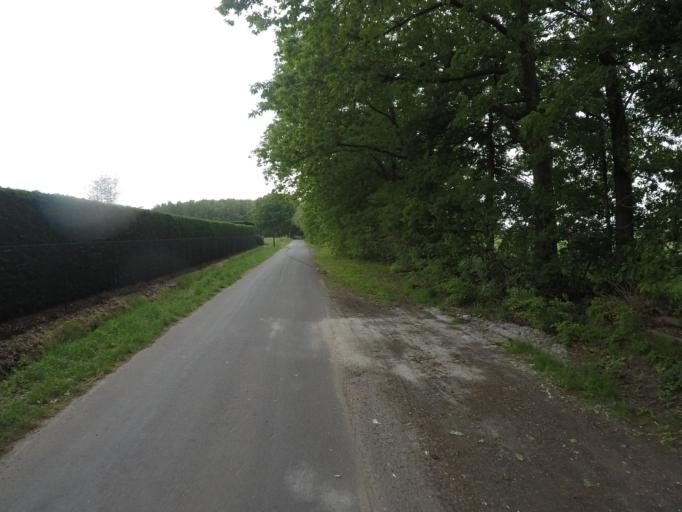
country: BE
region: Flanders
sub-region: Provincie Antwerpen
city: Oostmalle
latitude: 51.2922
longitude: 4.7190
